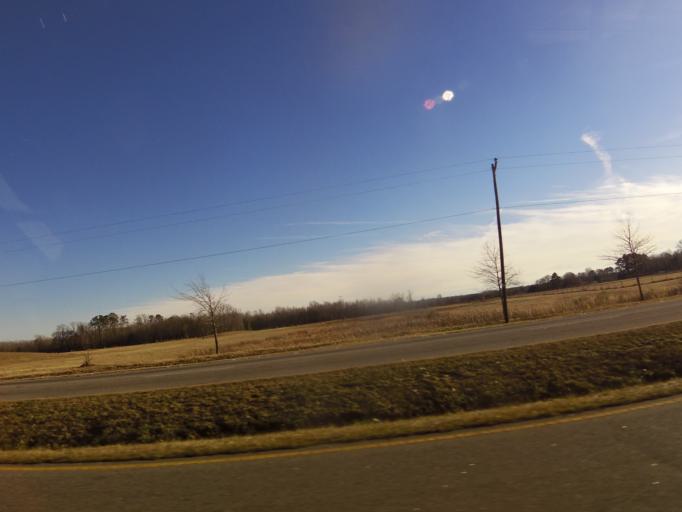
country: US
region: Virginia
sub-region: Isle of Wight County
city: Windsor
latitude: 36.6923
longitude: -76.7399
